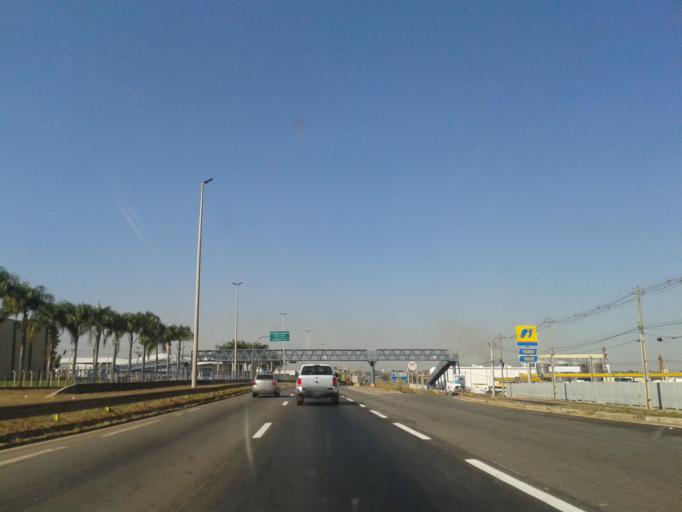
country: BR
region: Goias
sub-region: Aparecida De Goiania
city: Aparecida de Goiania
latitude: -16.8028
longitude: -49.2392
